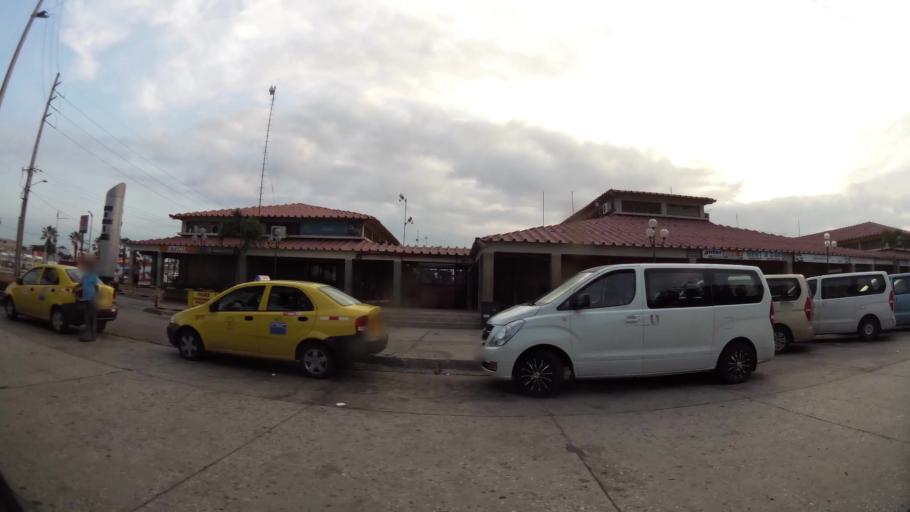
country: EC
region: Guayas
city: Eloy Alfaro
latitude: -2.1442
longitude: -79.8843
